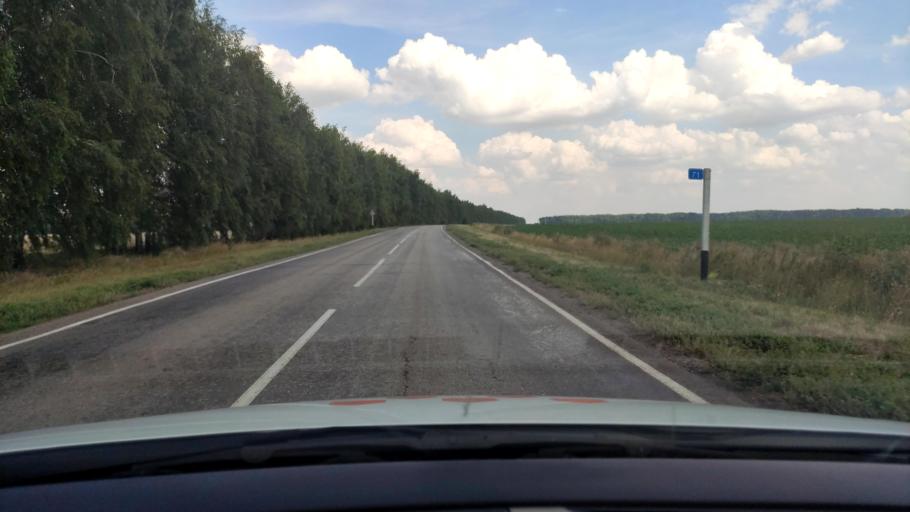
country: RU
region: Voronezj
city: Ertil'
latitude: 51.7879
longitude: 40.6026
